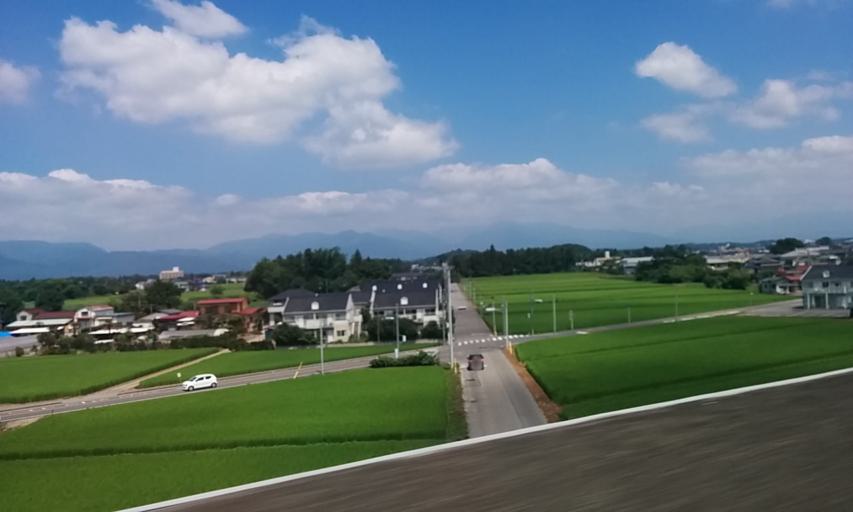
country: JP
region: Tochigi
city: Otawara
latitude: 36.8710
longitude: 139.9770
